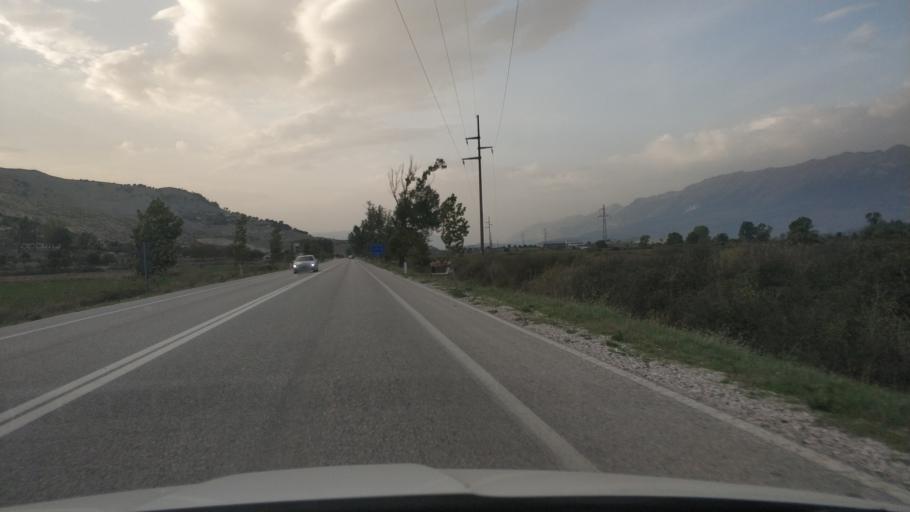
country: AL
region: Gjirokaster
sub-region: Rrethi i Gjirokastres
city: Libohove
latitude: 39.9632
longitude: 20.2431
